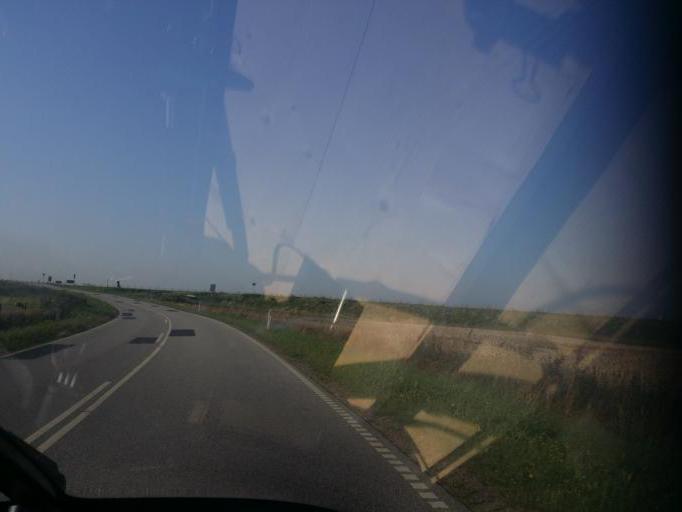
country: DE
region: Schleswig-Holstein
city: Rodenas
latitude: 54.9584
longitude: 8.7013
